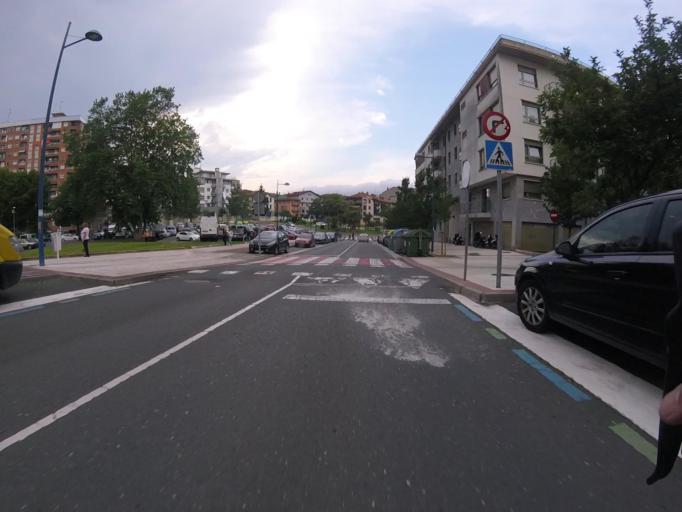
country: ES
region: Basque Country
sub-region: Provincia de Guipuzcoa
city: Errenteria
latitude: 43.3099
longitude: -1.9025
